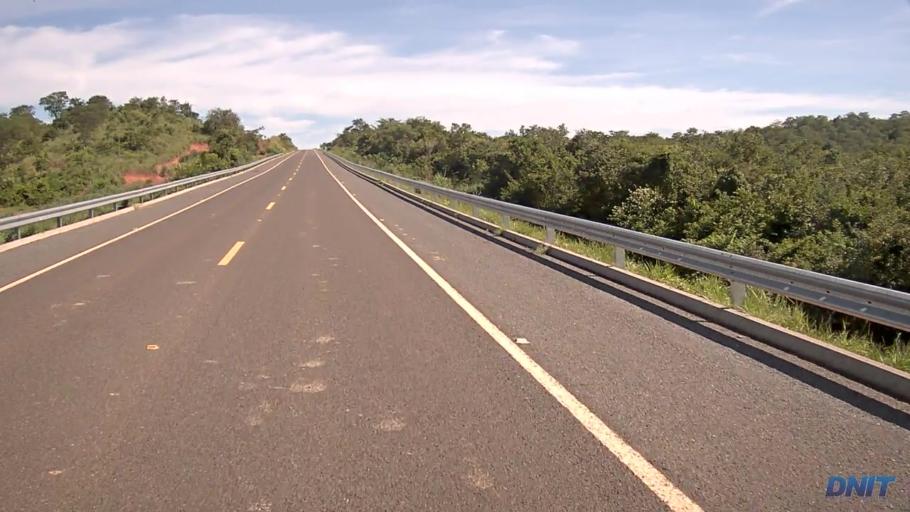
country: BR
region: Goias
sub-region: Sao Miguel Do Araguaia
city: Sao Miguel do Araguaia
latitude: -13.3330
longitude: -50.1544
